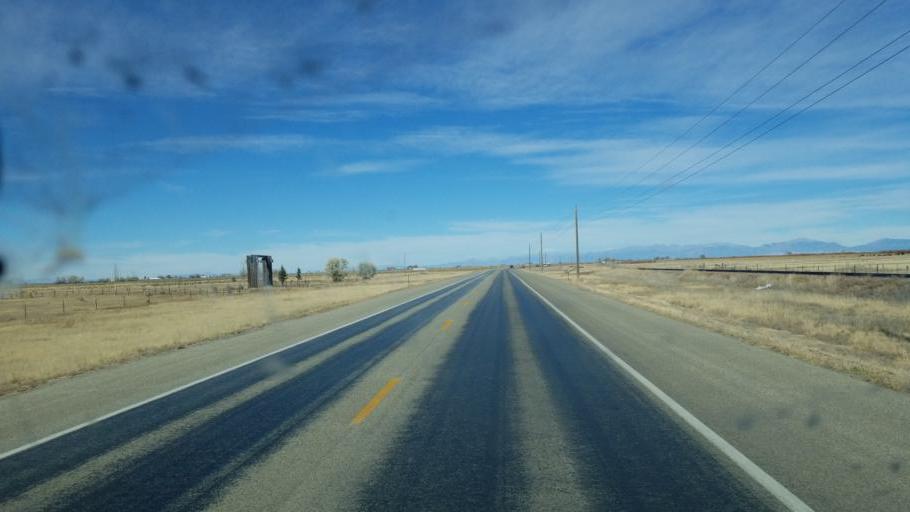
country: US
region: Colorado
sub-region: Alamosa County
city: Alamosa
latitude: 37.3152
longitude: -105.9505
